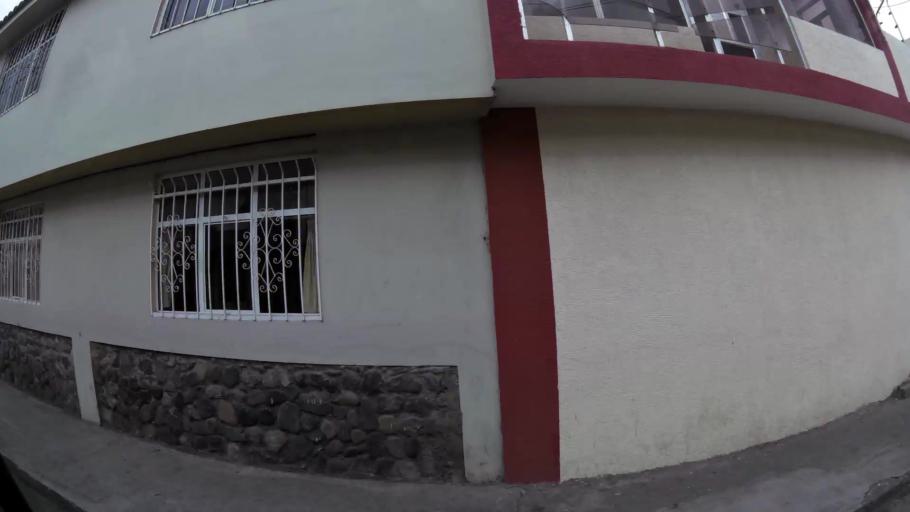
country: EC
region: Cotopaxi
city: Latacunga
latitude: -0.9314
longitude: -78.6250
